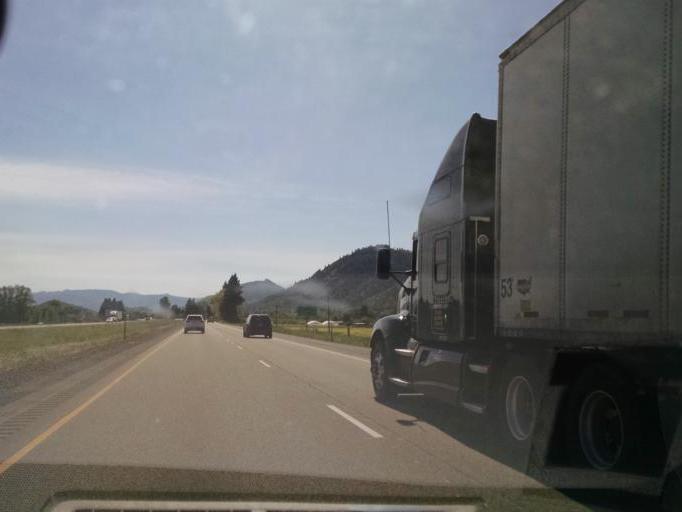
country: US
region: Oregon
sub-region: Douglas County
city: Tri-City
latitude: 42.9987
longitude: -123.3189
